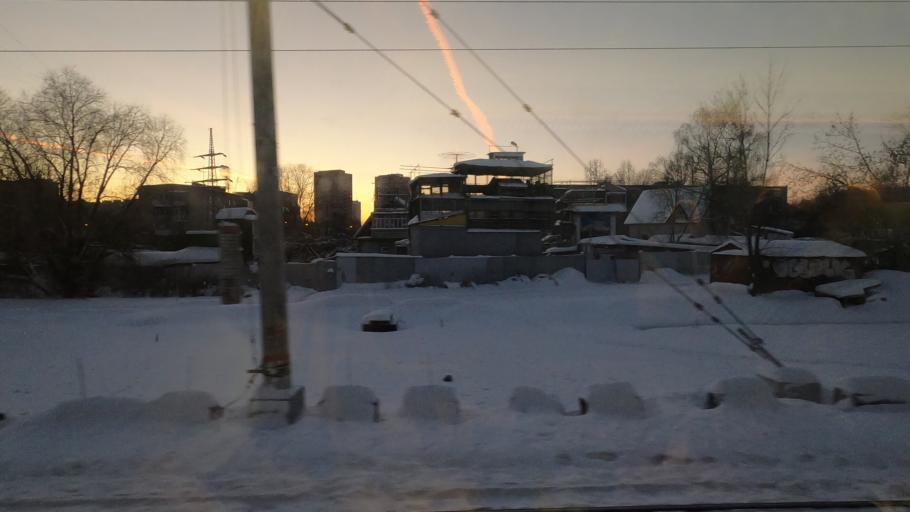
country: RU
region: Moskovskaya
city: Lobnya
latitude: 56.0070
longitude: 37.4879
